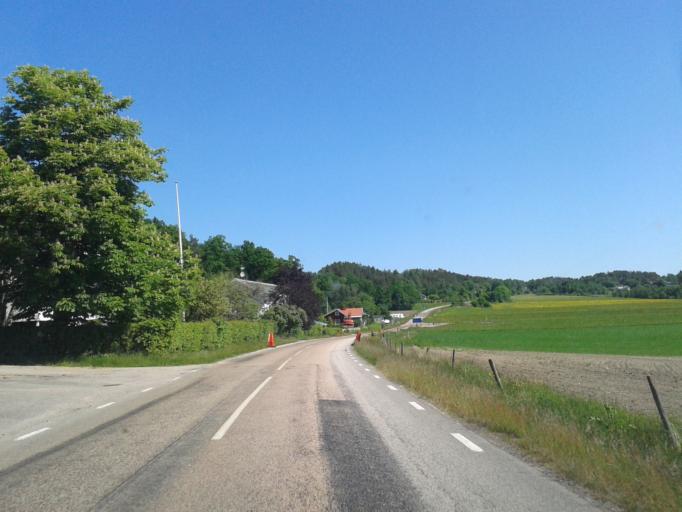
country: SE
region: Vaestra Goetaland
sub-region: Orust
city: Henan
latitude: 58.2578
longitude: 11.7292
